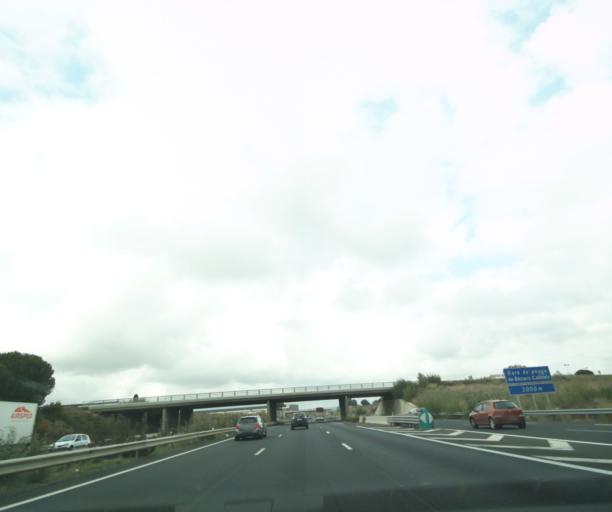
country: FR
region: Languedoc-Roussillon
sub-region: Departement de l'Herault
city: Villeneuve-les-Beziers
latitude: 43.3330
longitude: 3.2833
